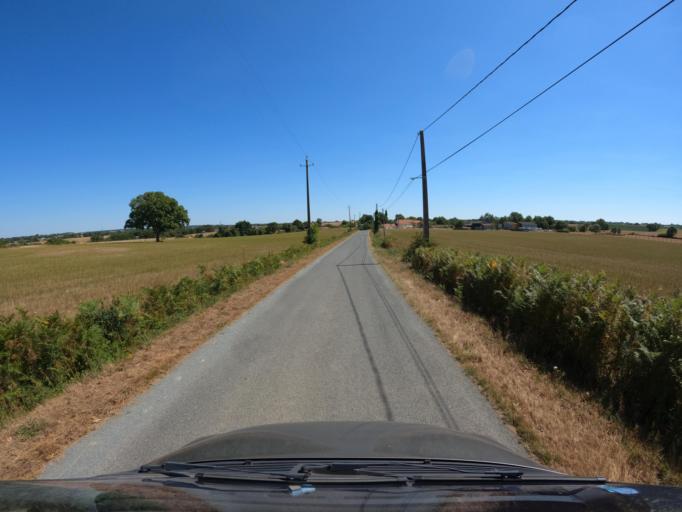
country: FR
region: Pays de la Loire
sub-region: Departement de Maine-et-Loire
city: Saint-Christophe-du-Bois
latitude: 47.0434
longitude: -0.9551
